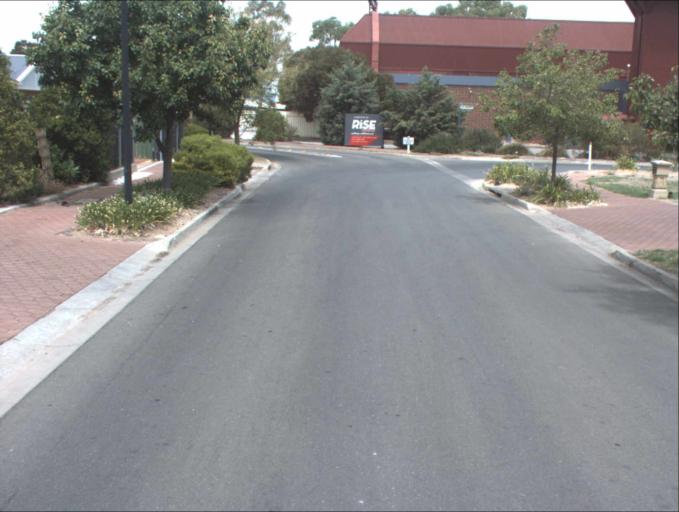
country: AU
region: South Australia
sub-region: Port Adelaide Enfield
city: Enfield
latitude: -34.8594
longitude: 138.6234
